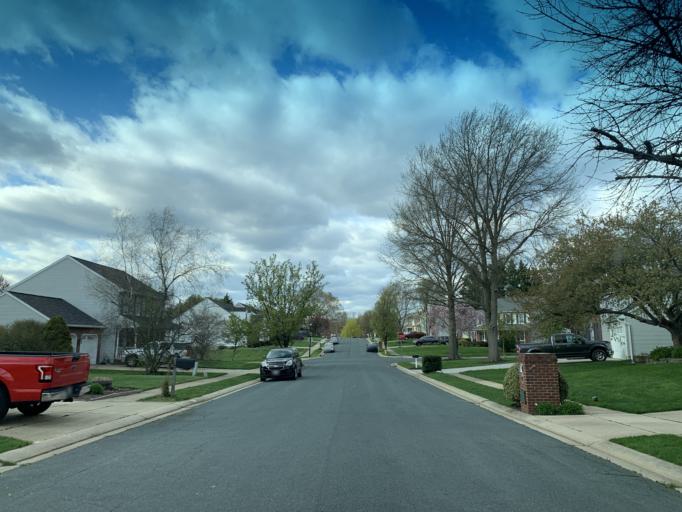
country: US
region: Maryland
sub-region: Harford County
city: South Bel Air
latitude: 39.5486
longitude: -76.3213
